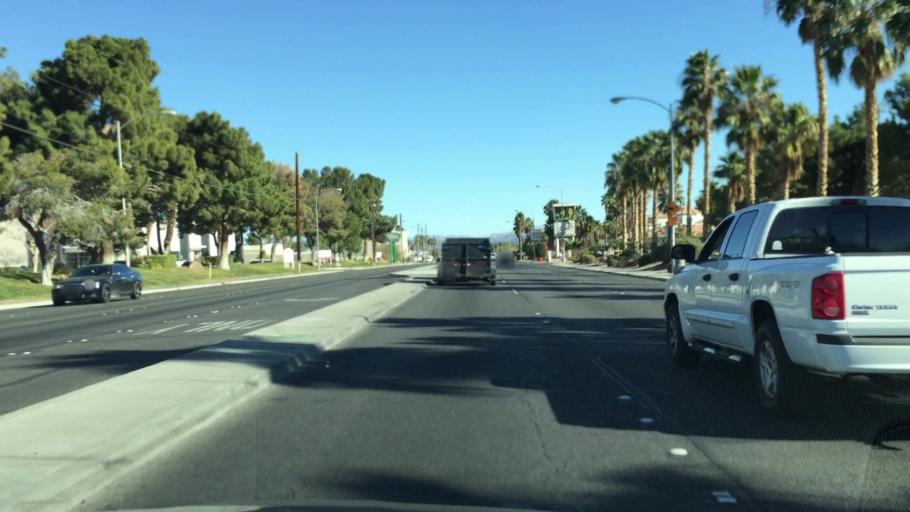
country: US
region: Nevada
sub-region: Clark County
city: Whitney
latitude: 36.0715
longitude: -115.1124
